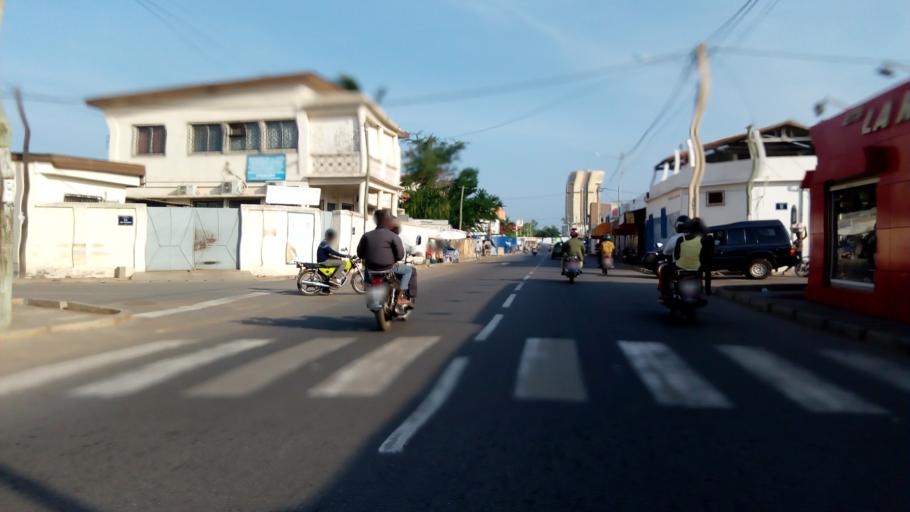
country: TG
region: Maritime
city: Lome
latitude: 6.1328
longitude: 1.2117
